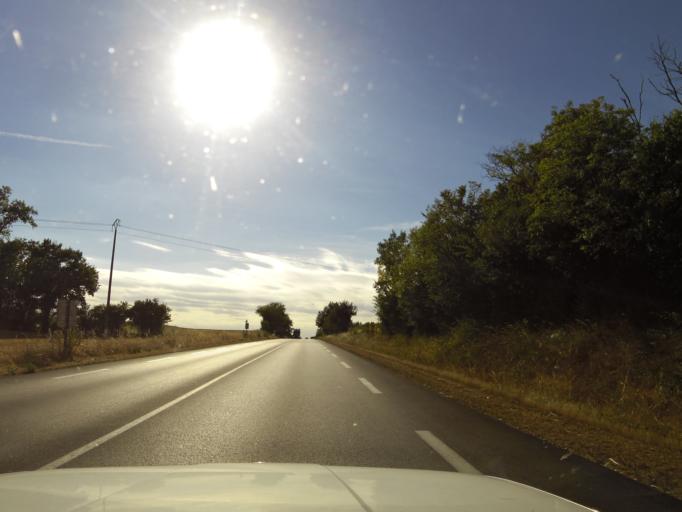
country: FR
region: Rhone-Alpes
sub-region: Departement de l'Ain
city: Saint-Jean-de-Niost
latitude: 45.8568
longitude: 5.2176
